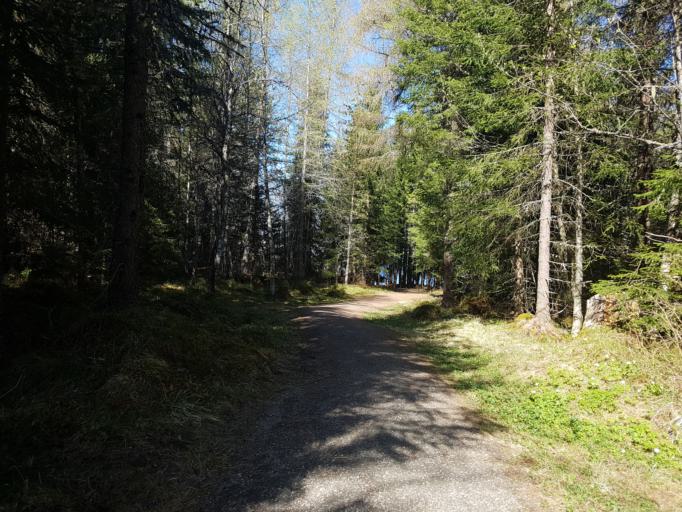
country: NO
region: Sor-Trondelag
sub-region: Trondheim
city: Trondheim
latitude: 63.4200
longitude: 10.3446
